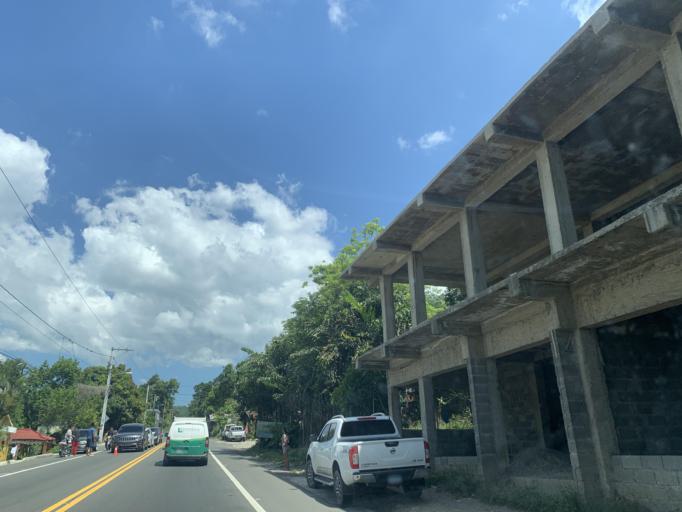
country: DO
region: Puerto Plata
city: Altamira
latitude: 19.6725
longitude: -70.8347
